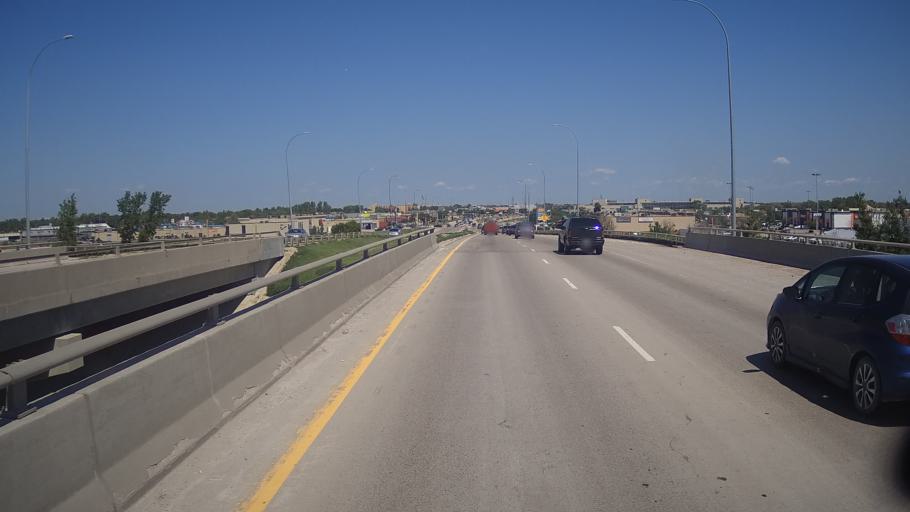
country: CA
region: Manitoba
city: Winnipeg
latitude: 49.8940
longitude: -97.0709
